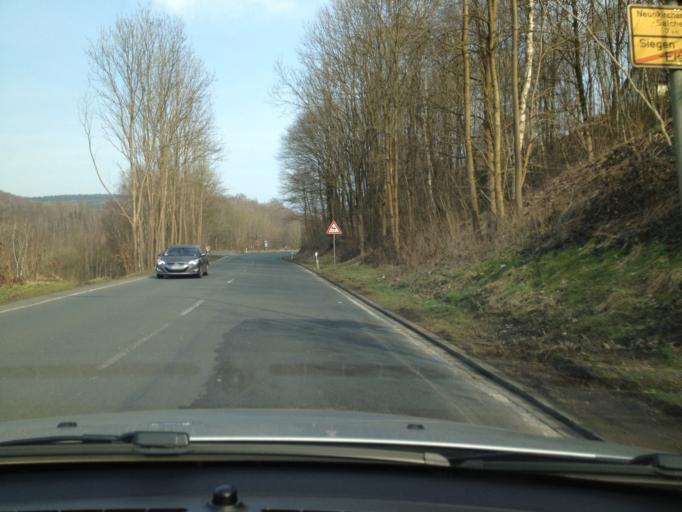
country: DE
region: North Rhine-Westphalia
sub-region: Regierungsbezirk Arnsberg
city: Neunkirchen
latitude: 50.8283
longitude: 8.0016
